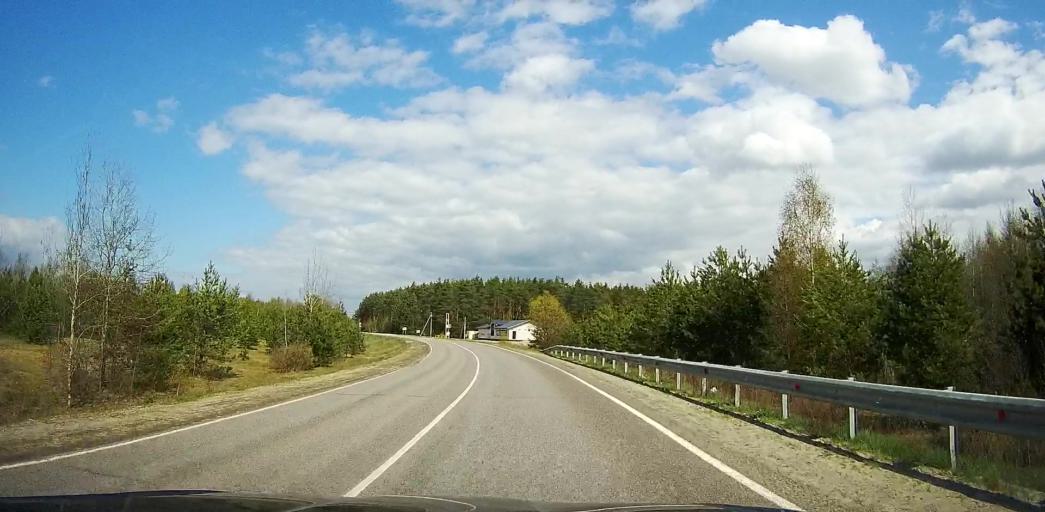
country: RU
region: Moskovskaya
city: Davydovo
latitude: 55.5481
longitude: 38.8161
